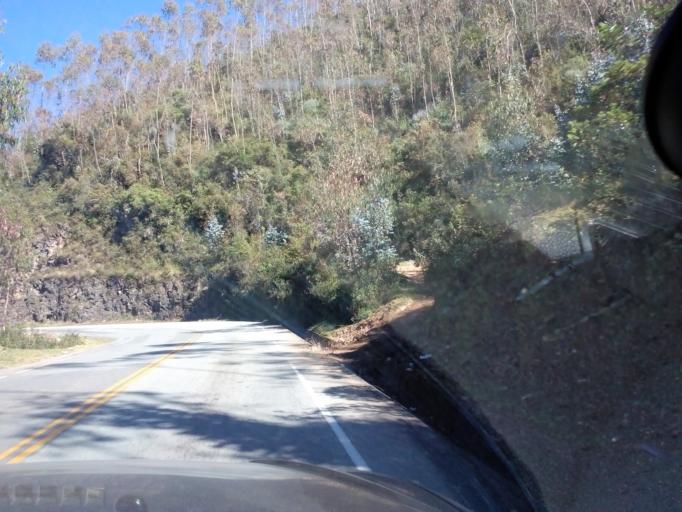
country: PE
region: Apurimac
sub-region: Provincia de Abancay
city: Tamburco
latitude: -13.5954
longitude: -72.8351
